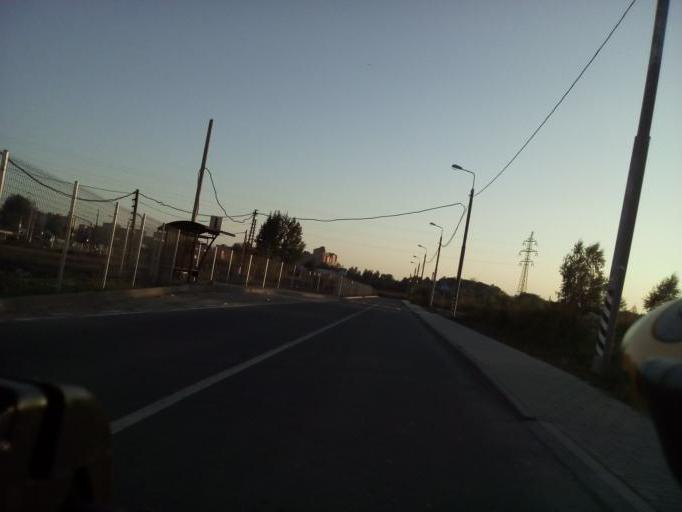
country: RU
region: Moskovskaya
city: Ramenskoye
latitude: 55.5897
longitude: 38.2506
